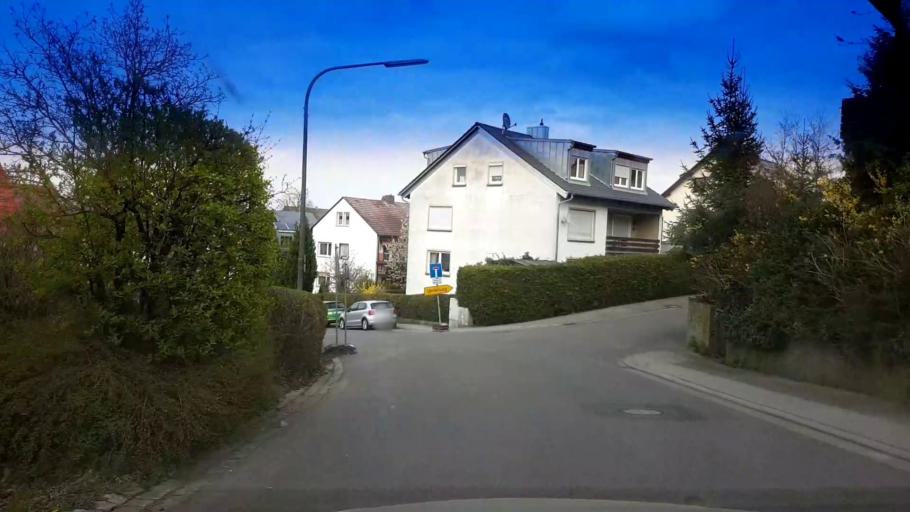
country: DE
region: Bavaria
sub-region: Upper Franconia
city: Bischberg
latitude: 49.9059
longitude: 10.8381
